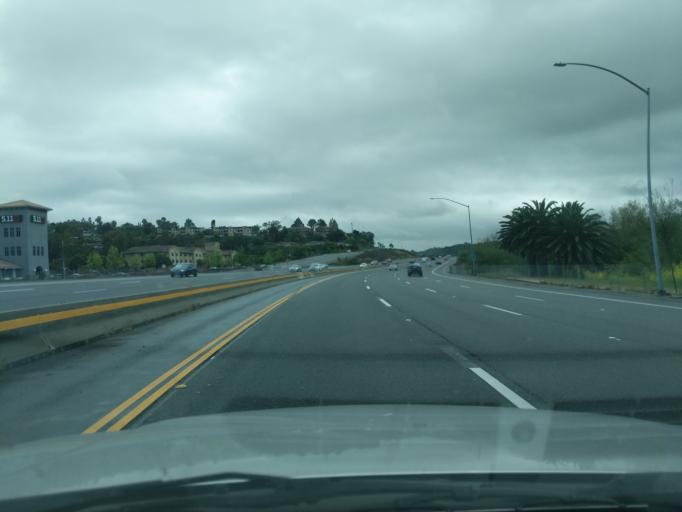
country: US
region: California
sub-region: San Diego County
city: Carlsbad
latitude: 33.1822
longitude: -117.3230
